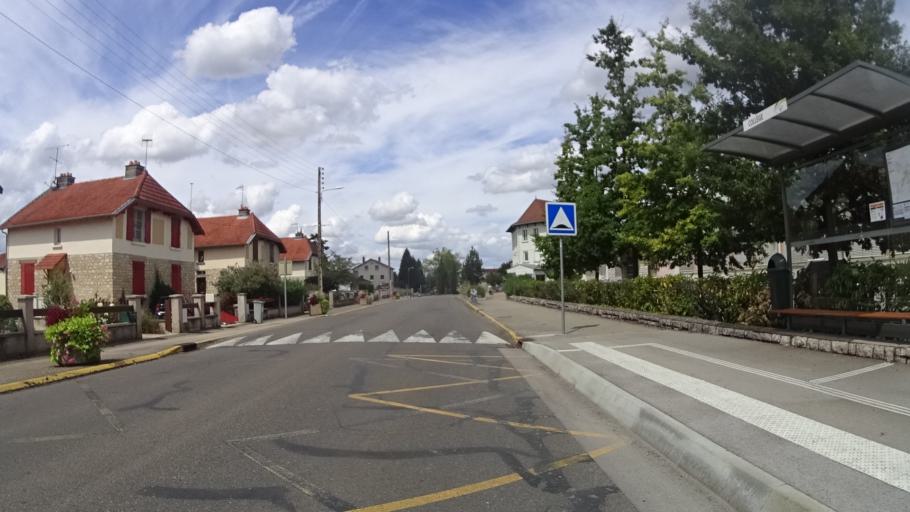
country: FR
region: Franche-Comte
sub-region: Departement du Jura
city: Damparis
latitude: 47.0688
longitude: 5.4138
